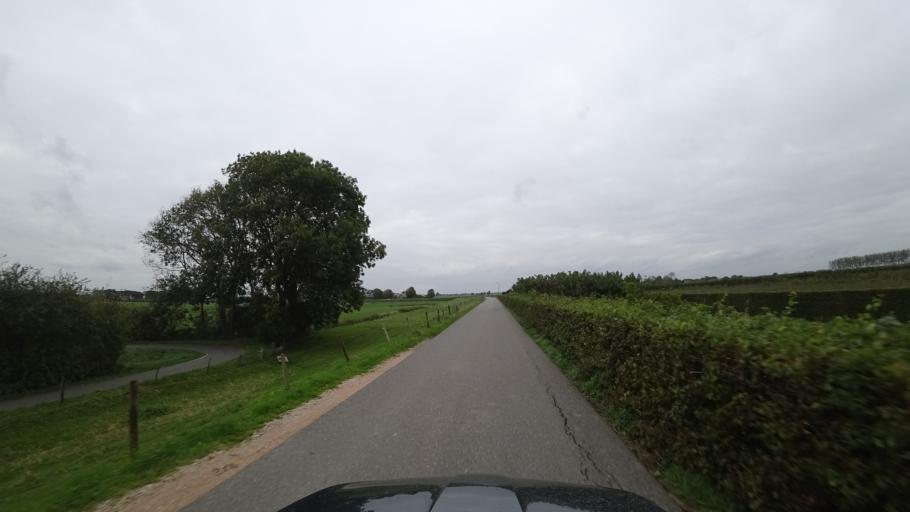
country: NL
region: Utrecht
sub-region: Gemeente De Ronde Venen
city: Mijdrecht
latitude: 52.2183
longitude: 4.8870
